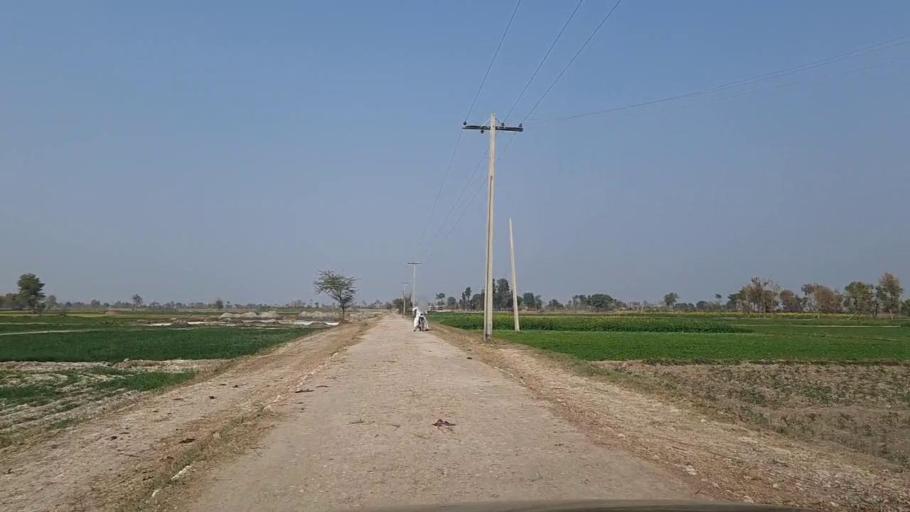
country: PK
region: Sindh
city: Daur
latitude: 26.4119
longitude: 68.4241
